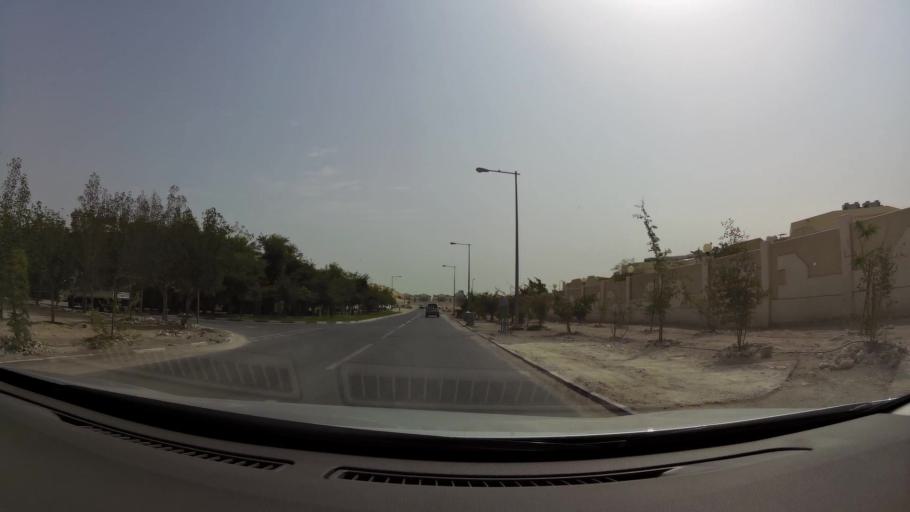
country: QA
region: Baladiyat ad Dawhah
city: Doha
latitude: 25.3022
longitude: 51.4785
